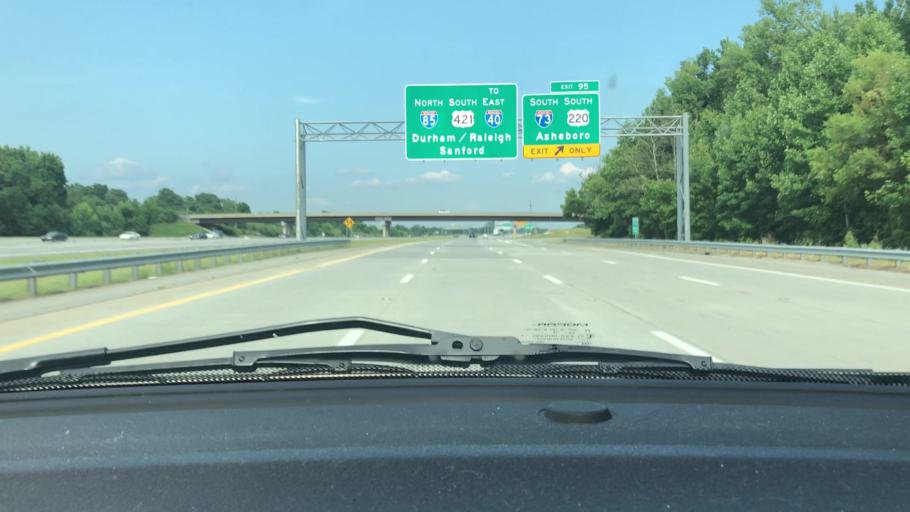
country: US
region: North Carolina
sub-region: Guilford County
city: Greensboro
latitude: 36.0033
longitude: -79.8366
